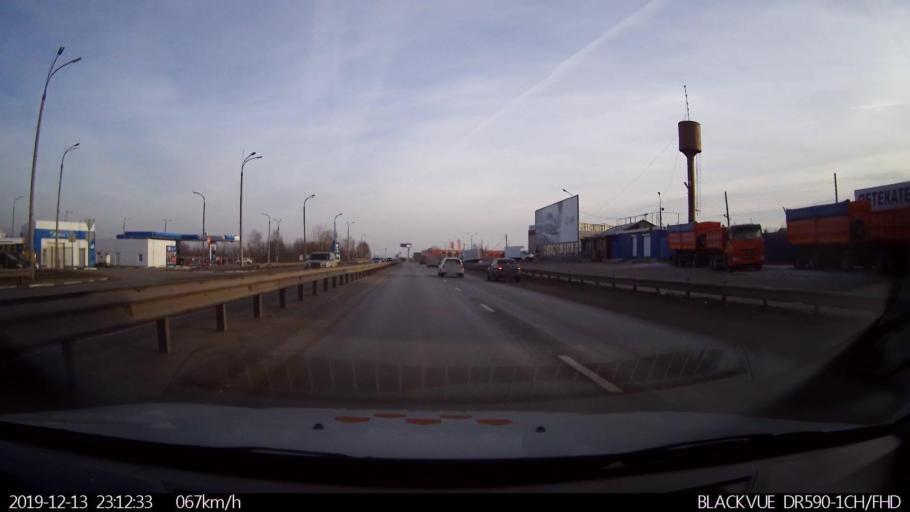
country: RU
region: Nizjnij Novgorod
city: Afonino
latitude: 56.2365
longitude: 44.0211
